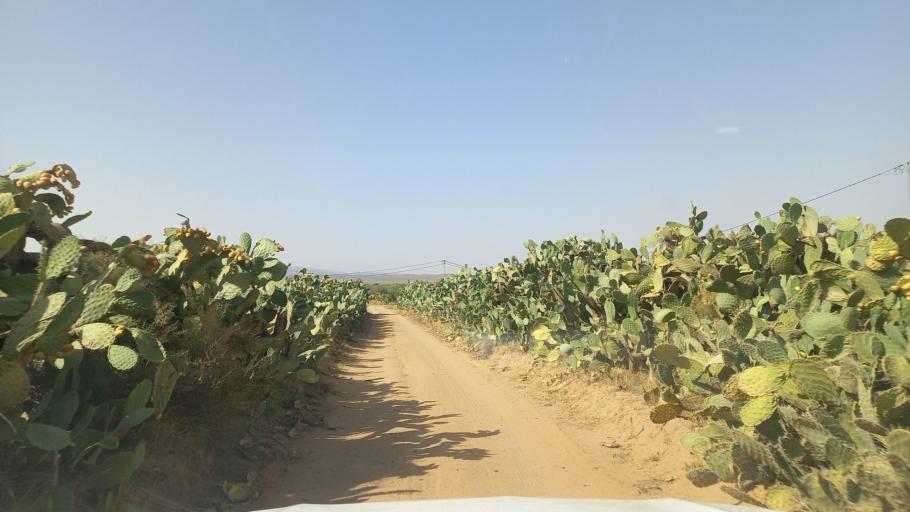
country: TN
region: Al Qasrayn
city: Kasserine
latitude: 35.2509
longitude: 9.0432
